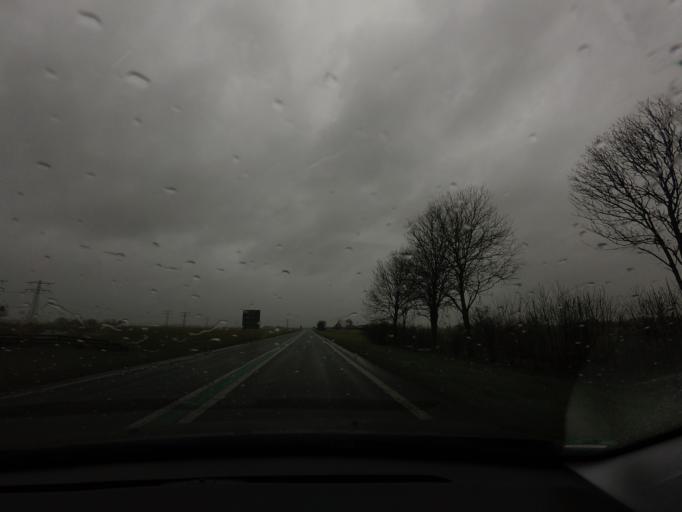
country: NL
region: Friesland
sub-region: Sudwest Fryslan
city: Bolsward
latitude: 53.0694
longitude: 5.5101
